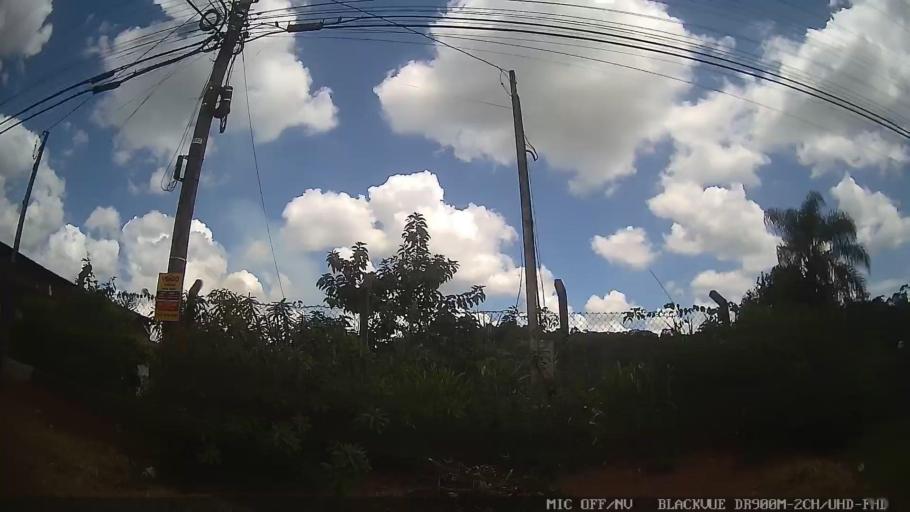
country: BR
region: Sao Paulo
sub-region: Atibaia
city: Atibaia
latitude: -23.1632
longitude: -46.6301
